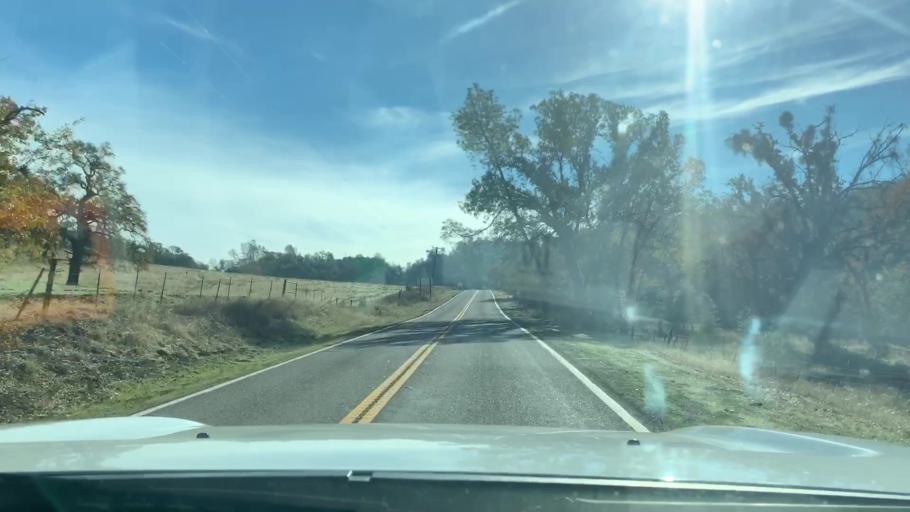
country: US
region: California
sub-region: Fresno County
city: Coalinga
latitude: 36.1709
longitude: -120.6693
